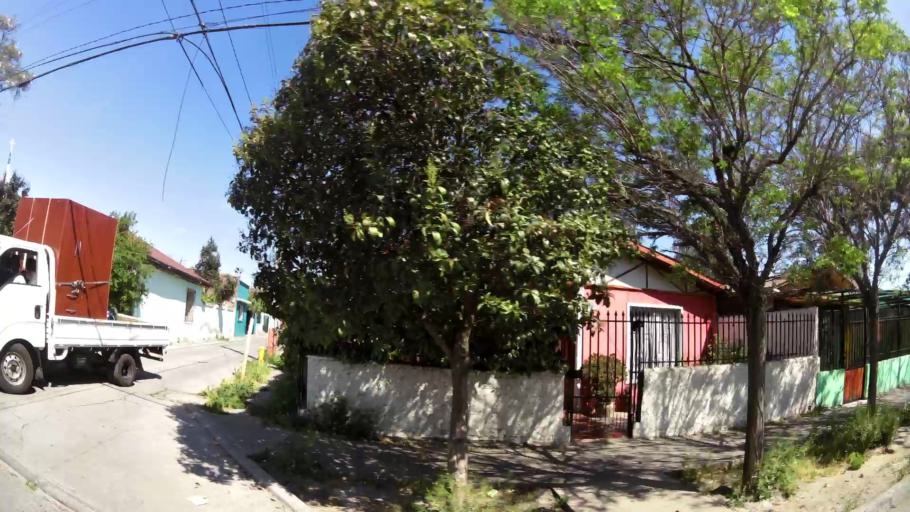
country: CL
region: Santiago Metropolitan
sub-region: Provincia de Santiago
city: Santiago
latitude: -33.5088
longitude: -70.6427
